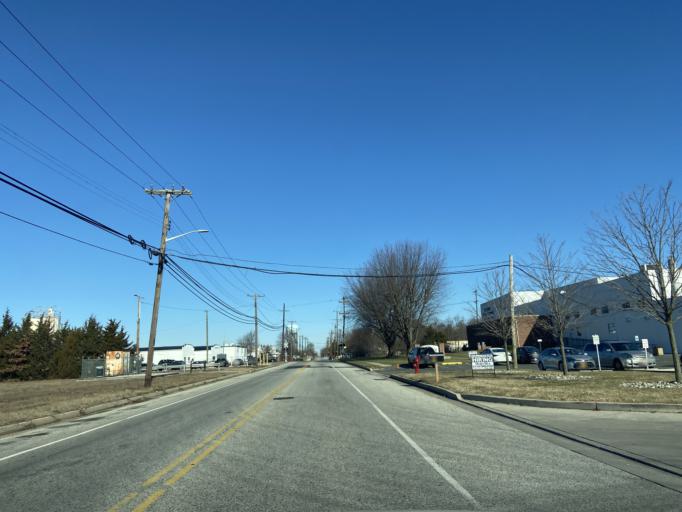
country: US
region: New Jersey
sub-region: Cumberland County
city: Vineland
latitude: 39.4903
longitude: -75.0613
